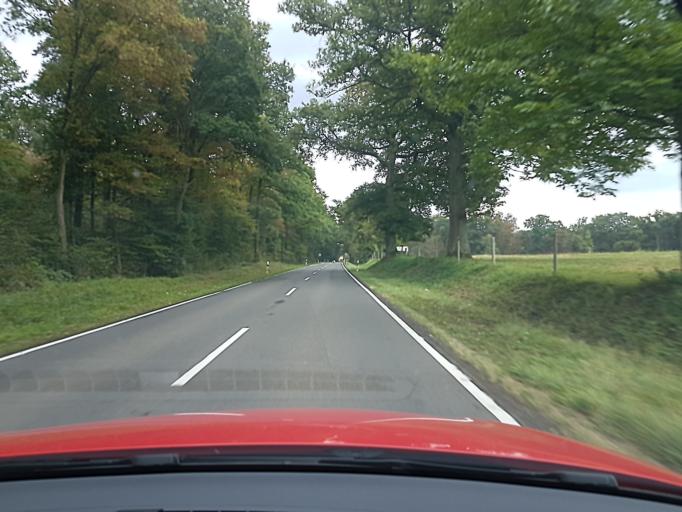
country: DE
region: Baden-Wuerttemberg
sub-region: Karlsruhe Region
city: Sternenfels
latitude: 49.0141
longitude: 8.8573
